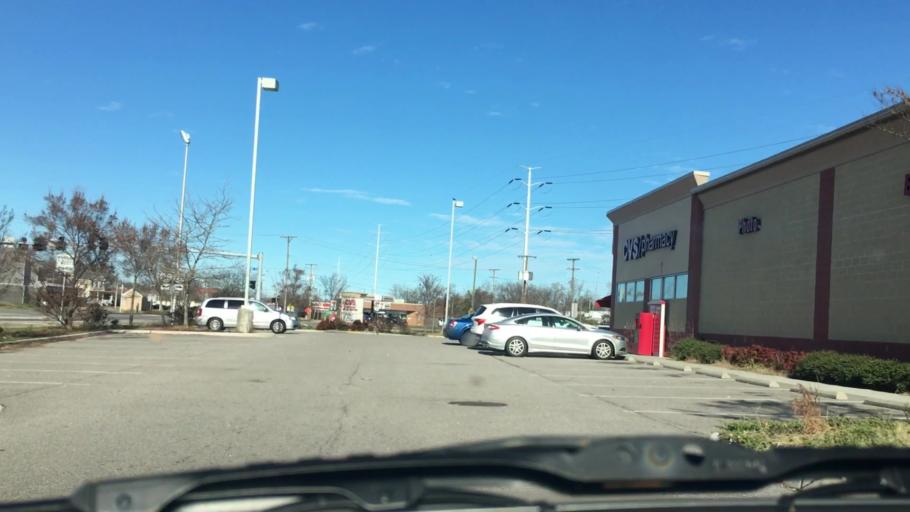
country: US
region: Virginia
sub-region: City of Norfolk
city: Norfolk
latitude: 36.8754
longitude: -76.2518
